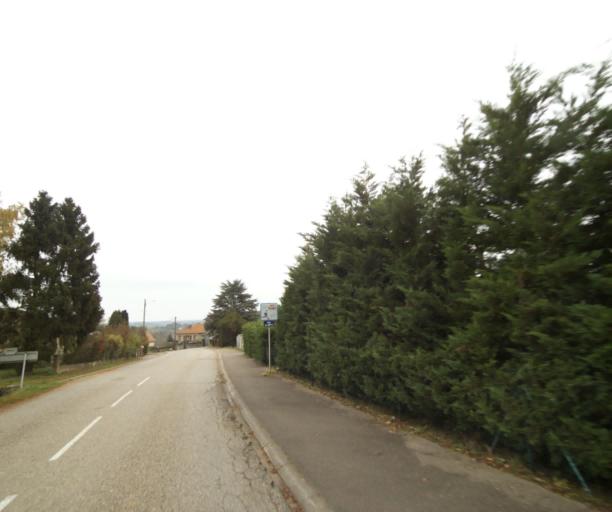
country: FR
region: Lorraine
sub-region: Departement de Meurthe-et-Moselle
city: Mancieulles
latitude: 49.2776
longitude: 5.8904
